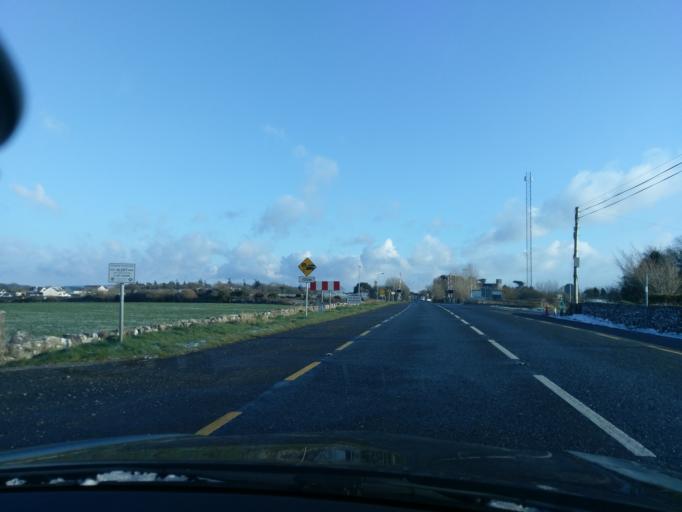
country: IE
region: Connaught
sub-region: County Galway
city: Gort
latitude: 53.1608
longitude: -8.8108
